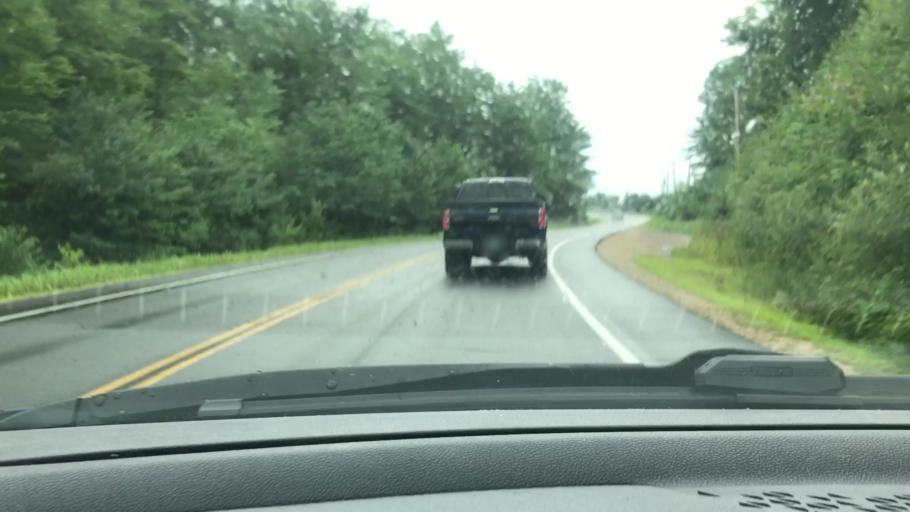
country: US
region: New Hampshire
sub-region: Rockingham County
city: Candia
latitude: 43.1382
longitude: -71.2361
